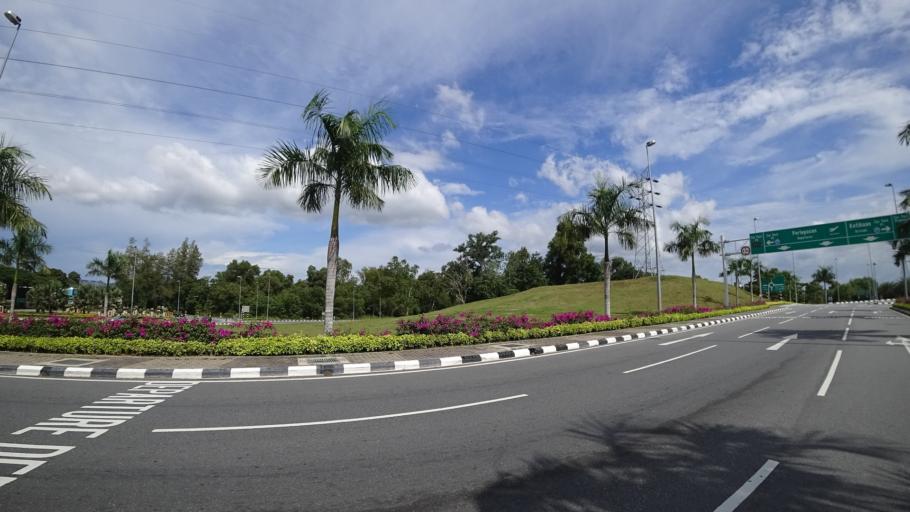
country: BN
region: Brunei and Muara
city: Bandar Seri Begawan
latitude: 4.9437
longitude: 114.9357
